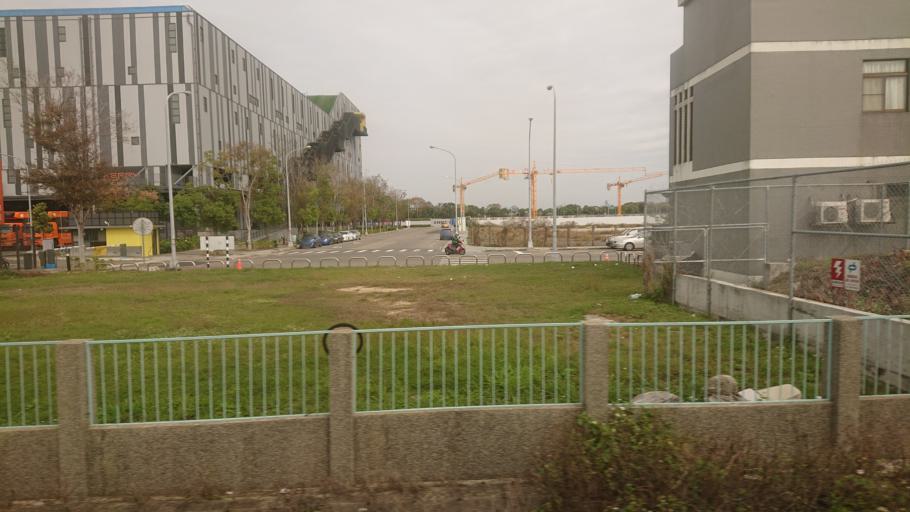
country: TW
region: Taiwan
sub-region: Changhua
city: Chang-hua
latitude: 24.1105
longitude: 120.6102
